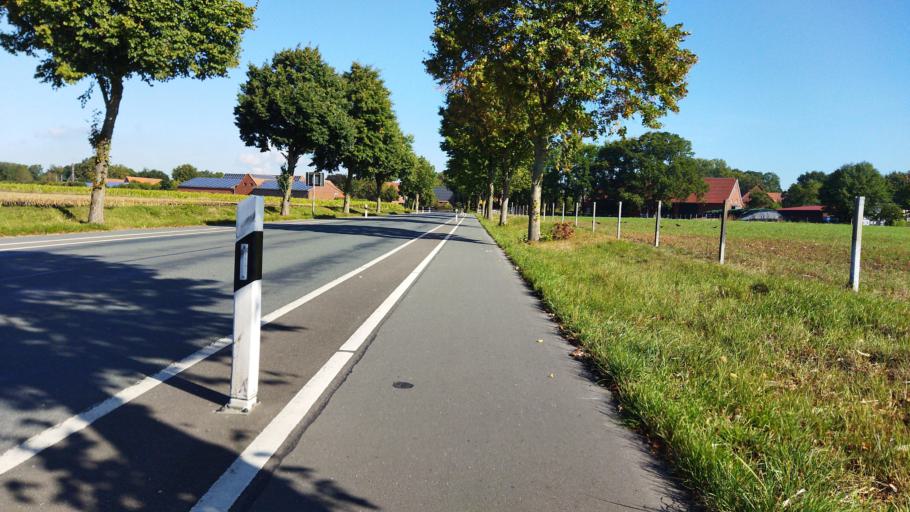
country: DE
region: Lower Saxony
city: Ohne
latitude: 52.2520
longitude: 7.3176
